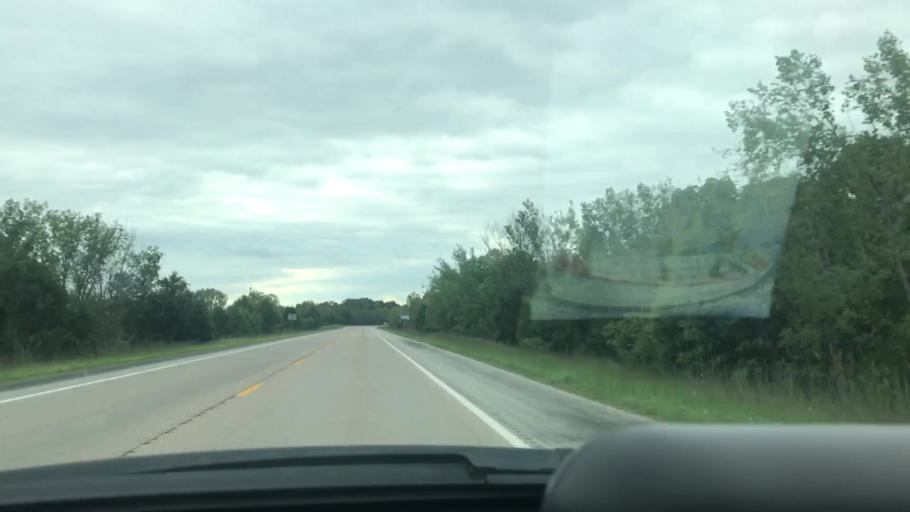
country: US
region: Missouri
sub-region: Benton County
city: Warsaw
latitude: 38.2107
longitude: -93.3385
